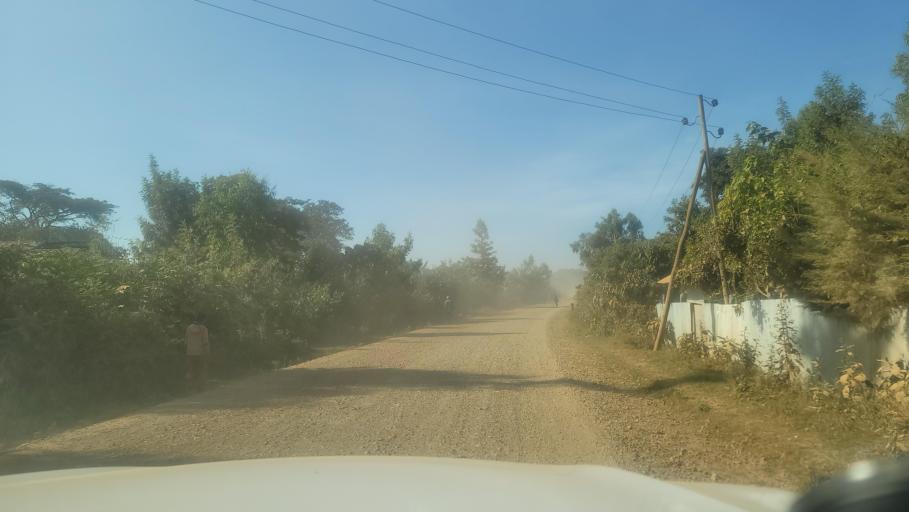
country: ET
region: Oromiya
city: Agaro
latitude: 7.8504
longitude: 36.5671
